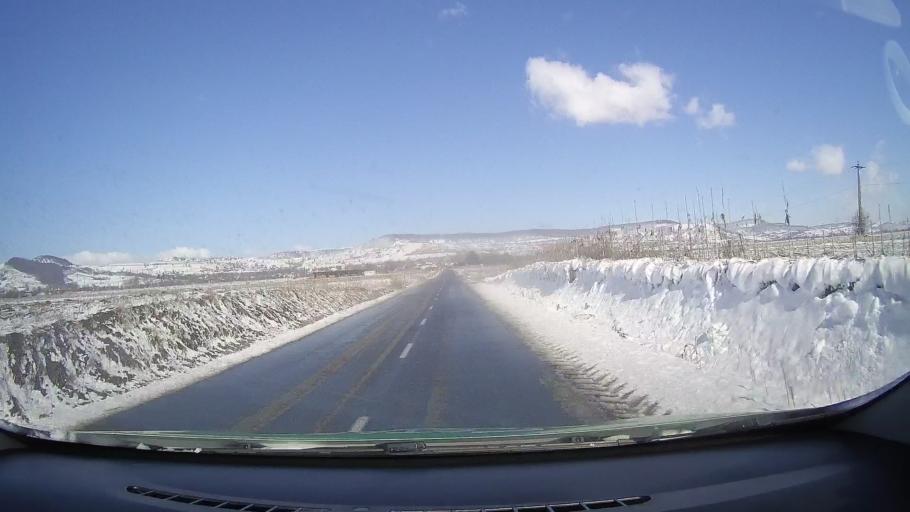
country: RO
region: Sibiu
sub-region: Comuna Avrig
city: Avrig
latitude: 45.7503
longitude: 24.3917
